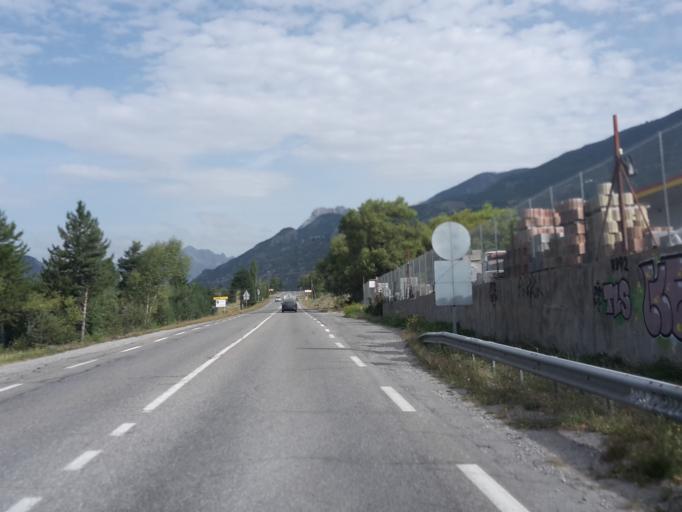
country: FR
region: Provence-Alpes-Cote d'Azur
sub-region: Departement des Hautes-Alpes
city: Guillestre
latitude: 44.6841
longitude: 6.6145
